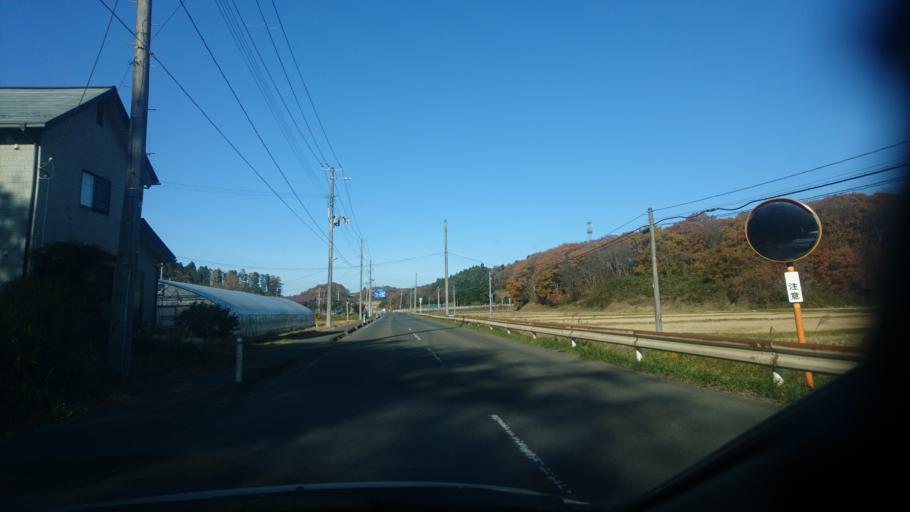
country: JP
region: Miyagi
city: Tomiya
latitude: 38.4594
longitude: 140.9043
